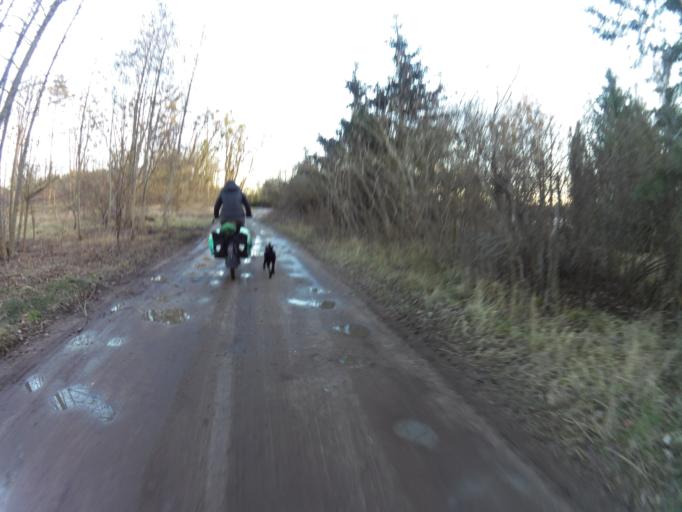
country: PL
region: West Pomeranian Voivodeship
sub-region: Powiat mysliborski
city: Debno
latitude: 52.8219
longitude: 14.7819
